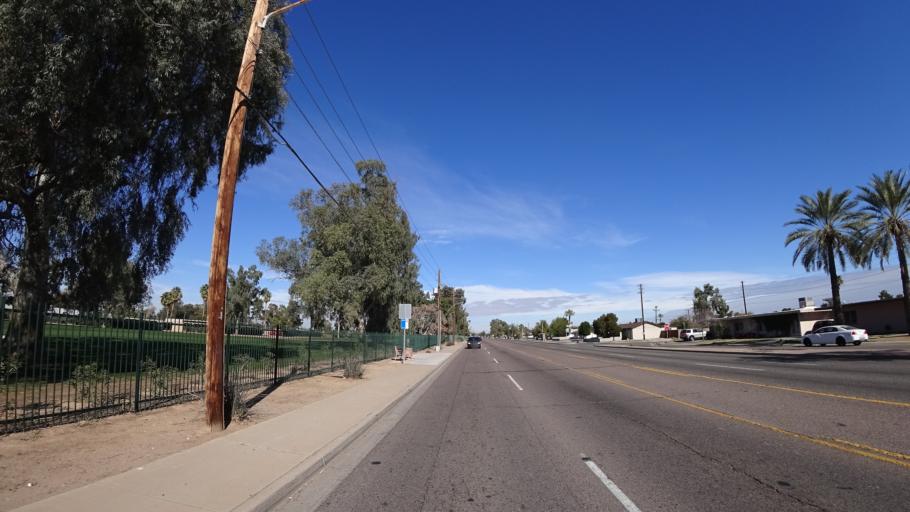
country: US
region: Arizona
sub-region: Maricopa County
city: Glendale
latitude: 33.4982
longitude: -112.1865
